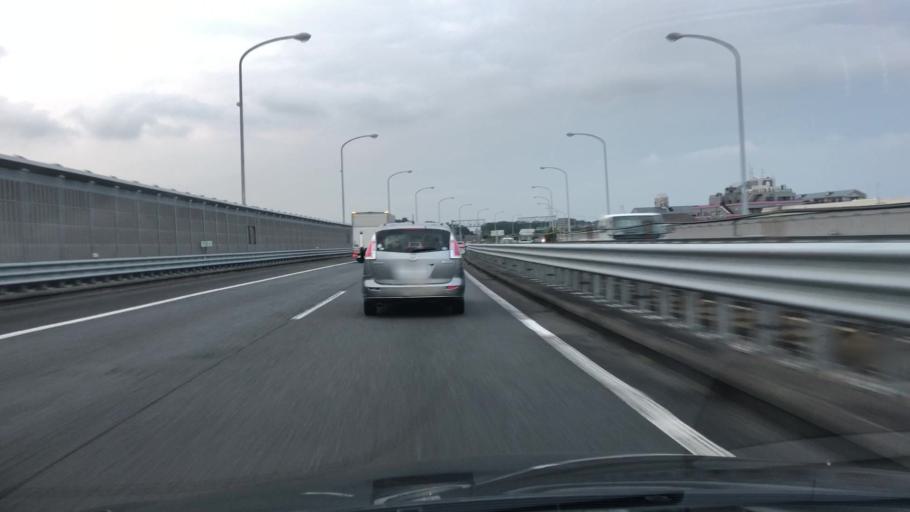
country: JP
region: Tokyo
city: Hino
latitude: 35.6787
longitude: 139.4232
